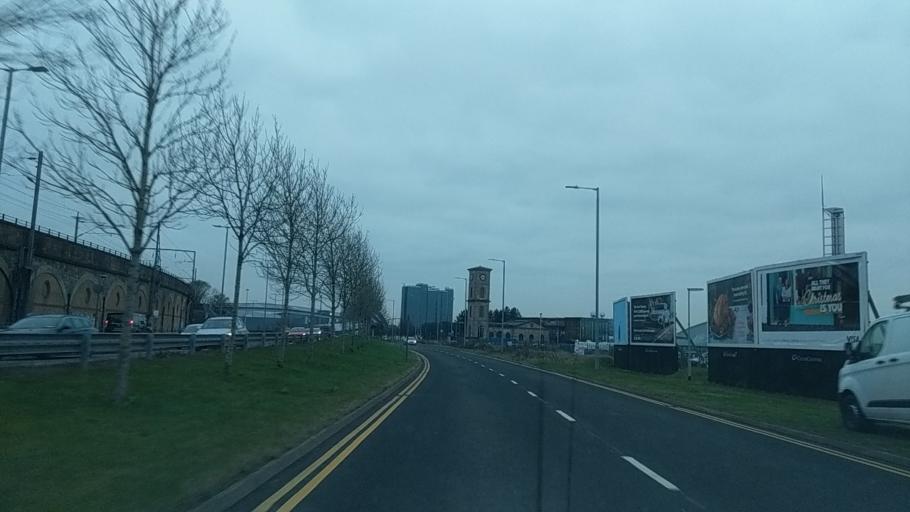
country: GB
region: Scotland
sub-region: Glasgow City
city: Glasgow
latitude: 55.8639
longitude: -4.2996
